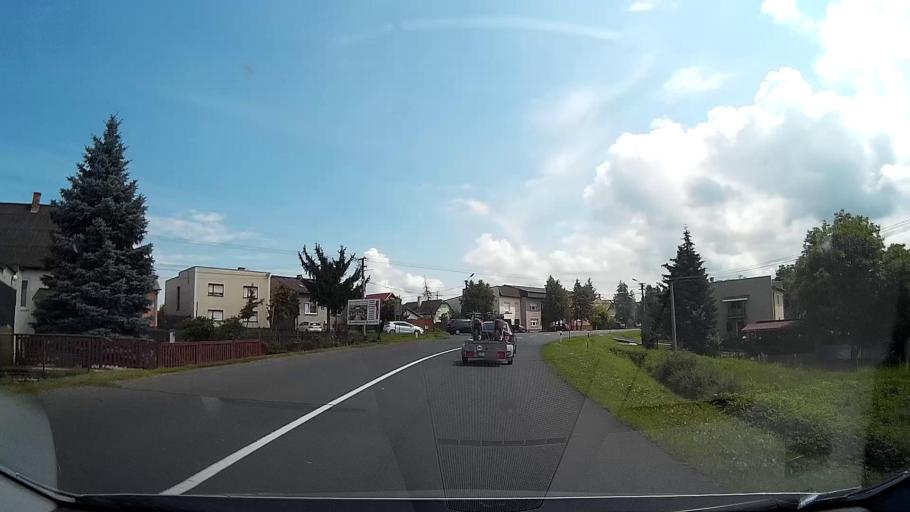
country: SK
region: Banskobystricky
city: Fil'akovo
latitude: 48.2553
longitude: 19.8304
